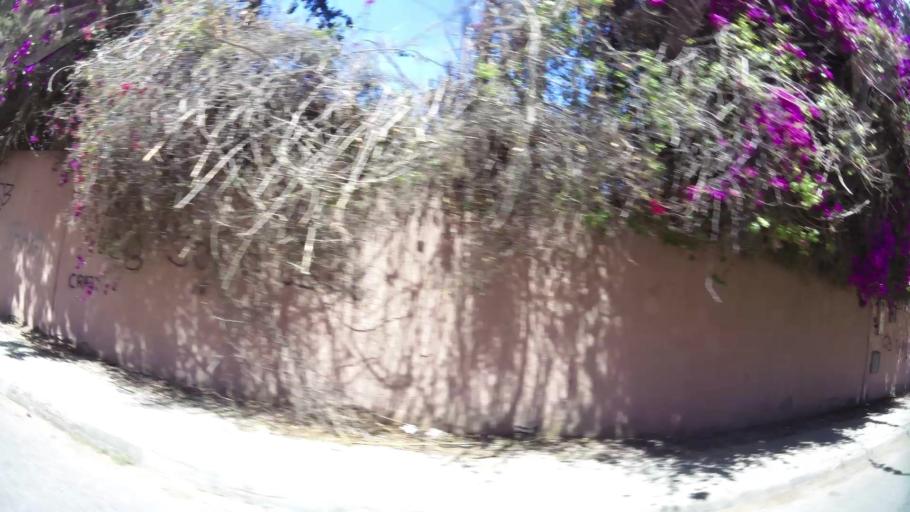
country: MA
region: Marrakech-Tensift-Al Haouz
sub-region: Marrakech
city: Marrakesh
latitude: 31.6424
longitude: -8.0523
